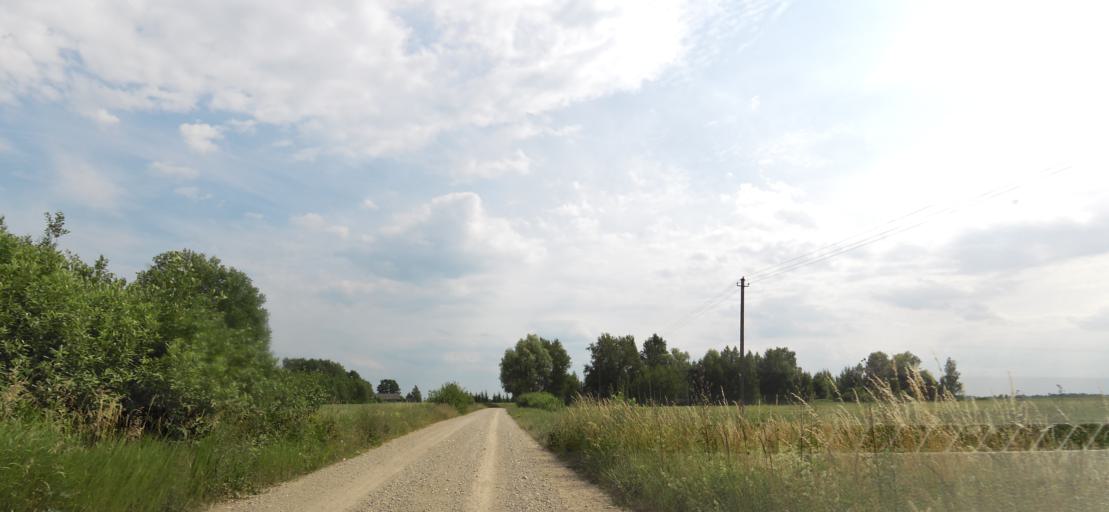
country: LT
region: Panevezys
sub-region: Birzai
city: Birzai
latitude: 56.1761
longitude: 24.9867
